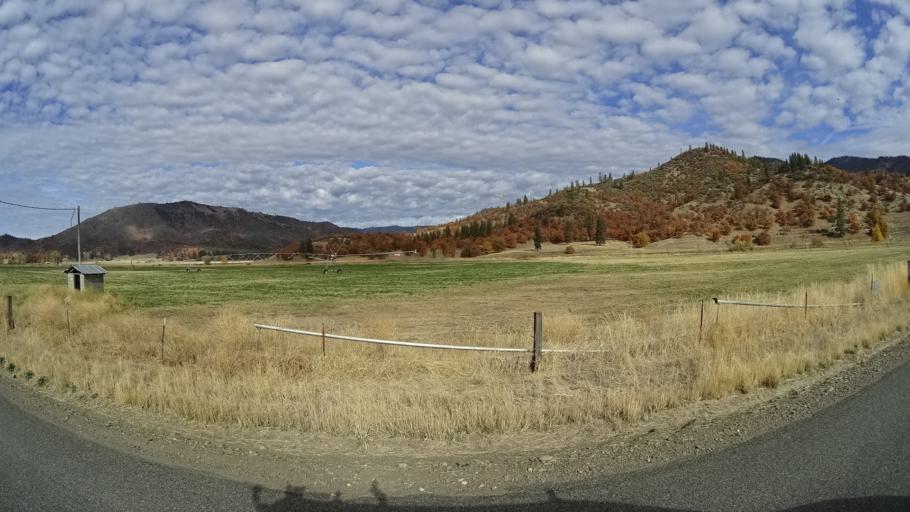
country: US
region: California
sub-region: Siskiyou County
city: Yreka
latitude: 41.6262
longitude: -122.8162
